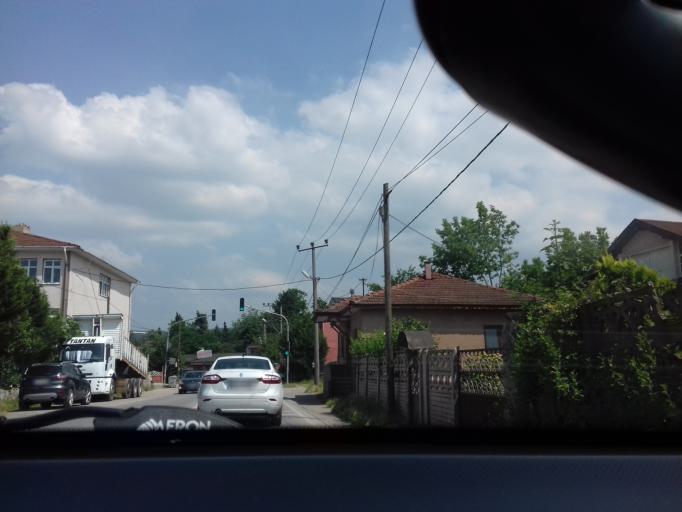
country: TR
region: Sakarya
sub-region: Merkez
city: Sapanca
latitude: 40.6877
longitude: 30.2669
